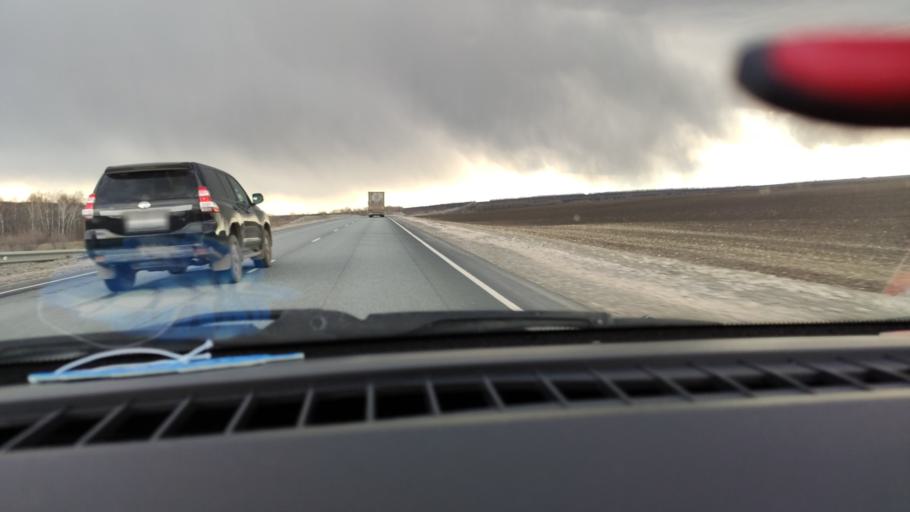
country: RU
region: Saratov
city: Yelshanka
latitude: 51.8582
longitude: 46.4966
